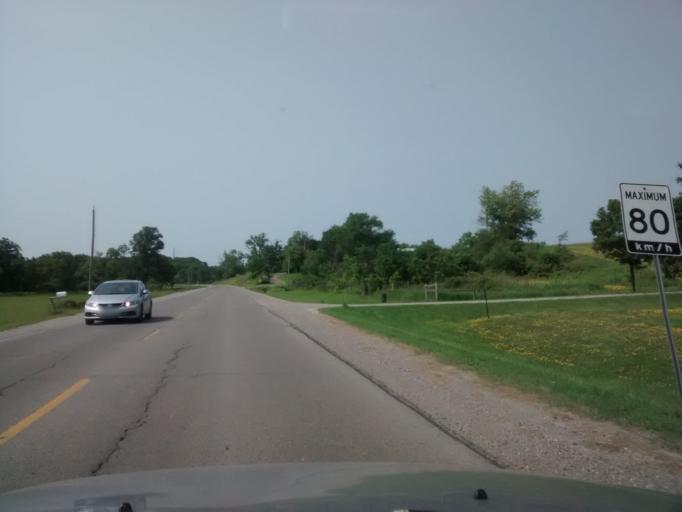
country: CA
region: Ontario
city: Ancaster
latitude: 42.9995
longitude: -79.8668
